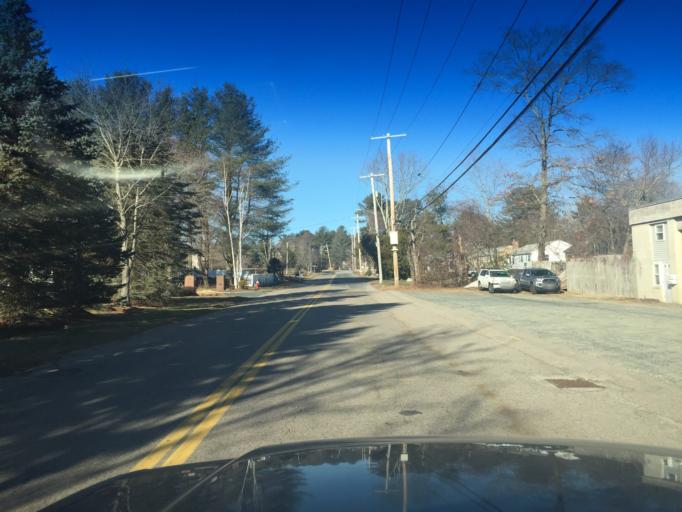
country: US
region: Massachusetts
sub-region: Middlesex County
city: Holliston
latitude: 42.2037
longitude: -71.4022
